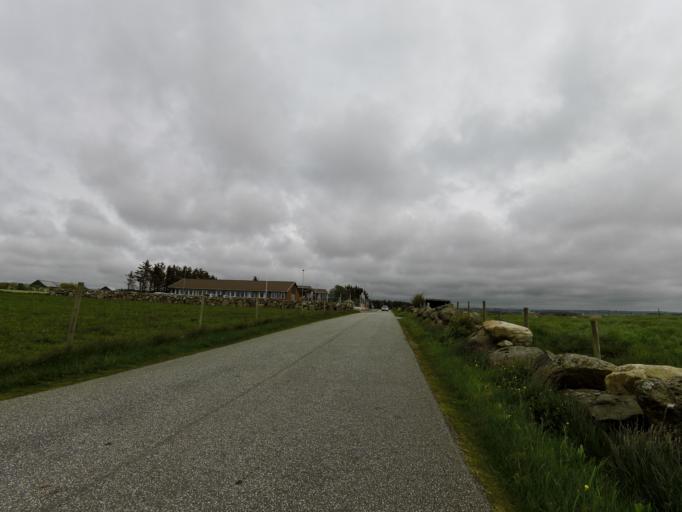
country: NO
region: Rogaland
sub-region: Ha
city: Naerbo
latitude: 58.6528
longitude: 5.5879
